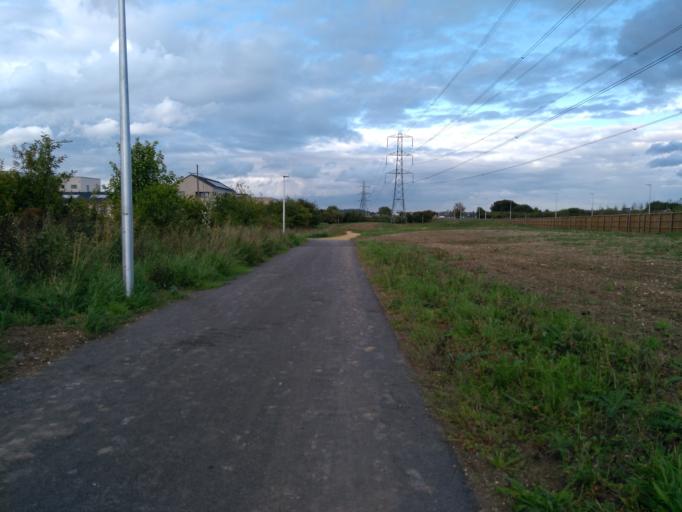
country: GB
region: England
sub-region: Central Bedfordshire
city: Houghton Regis
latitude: 51.9031
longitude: -0.5017
